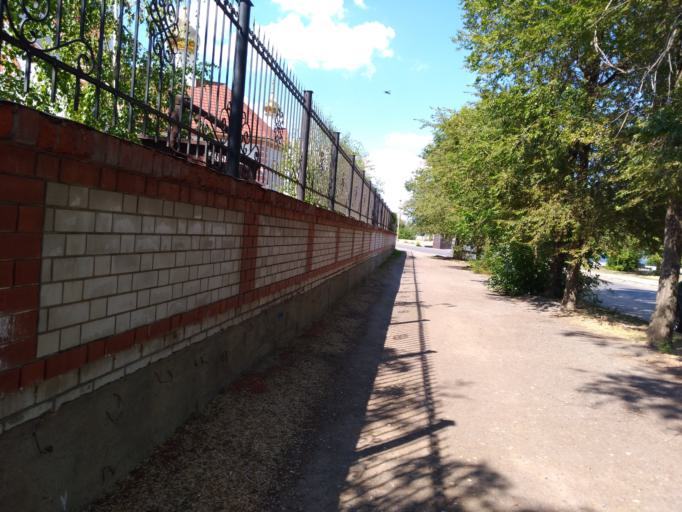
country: RU
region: Volgograd
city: Volgograd
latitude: 48.7197
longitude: 44.5380
